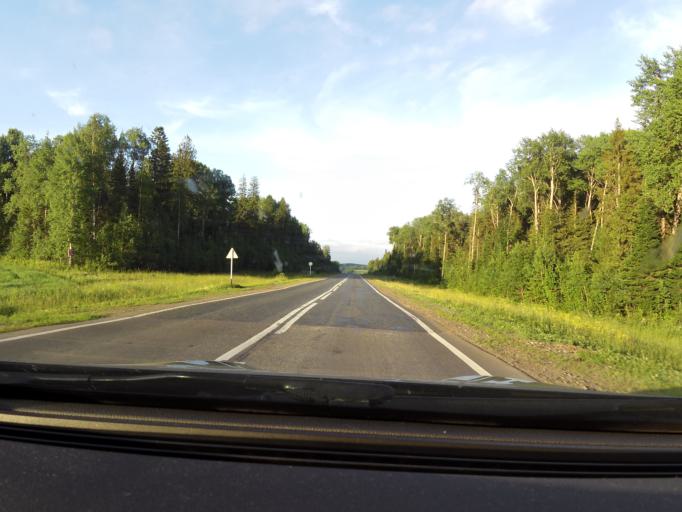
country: RU
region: Perm
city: Siva
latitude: 58.4869
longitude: 54.1592
